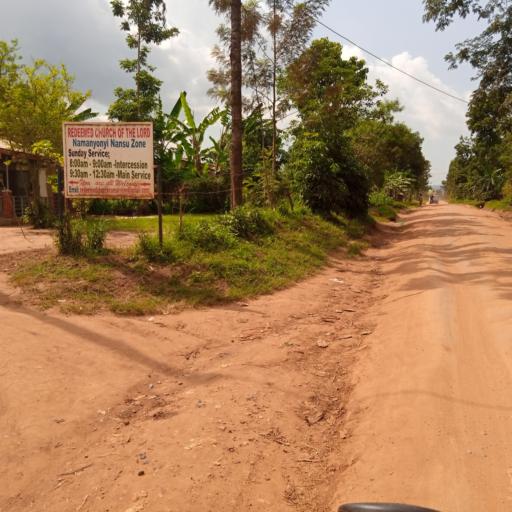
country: UG
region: Eastern Region
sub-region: Mbale District
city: Mbale
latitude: 1.1087
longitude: 34.2012
